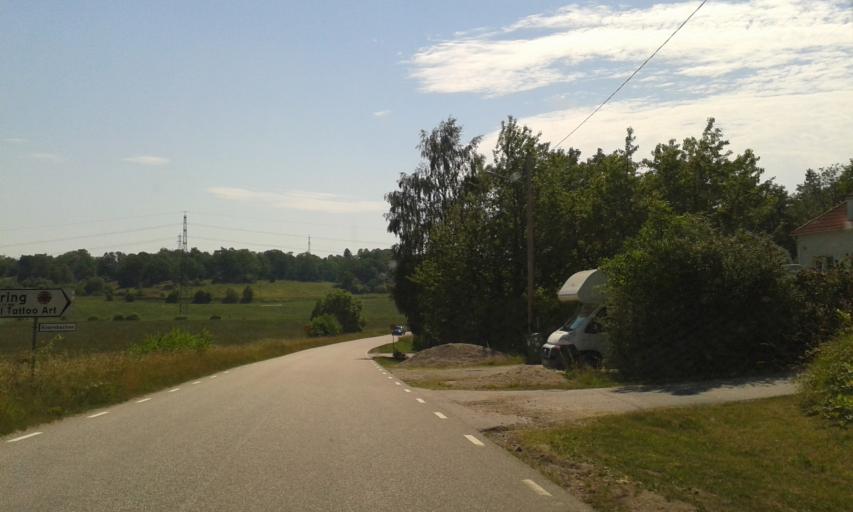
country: SE
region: Blekinge
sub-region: Karlskrona Kommun
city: Rodeby
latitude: 56.2280
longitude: 15.5856
